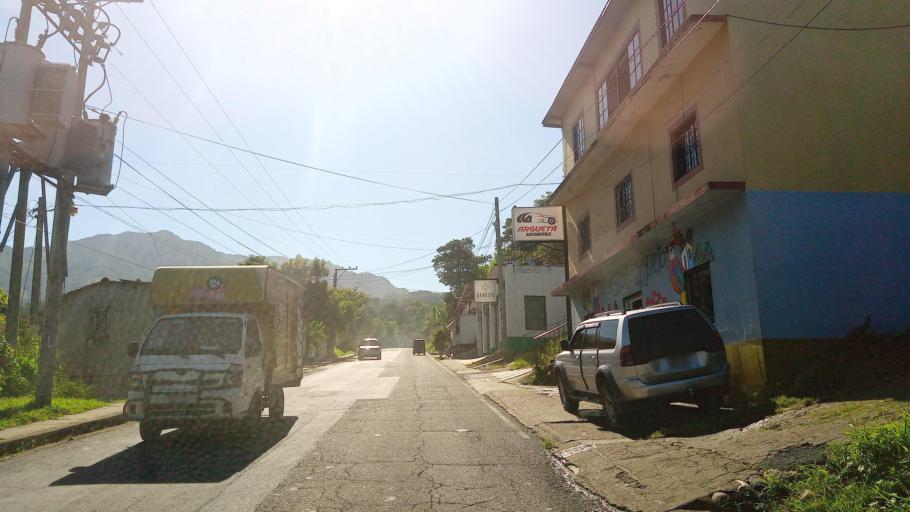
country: HN
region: Ocotepeque
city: Antigua Ocotepeque
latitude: 14.3141
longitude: -89.1649
